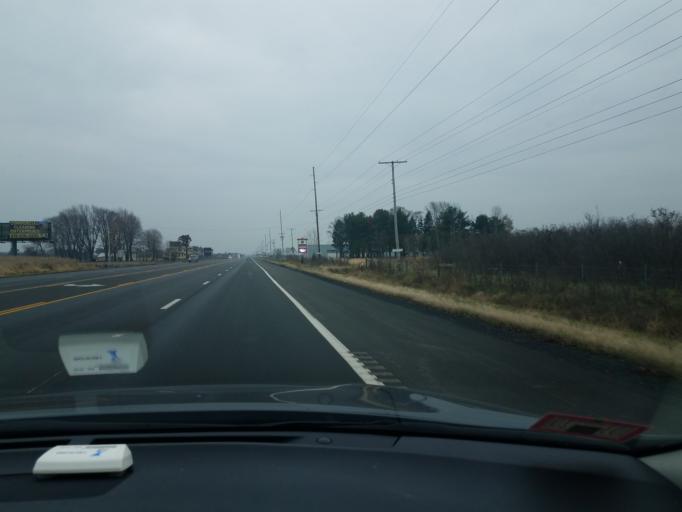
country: US
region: Ohio
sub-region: Erie County
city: Milan
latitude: 41.3700
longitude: -82.6407
